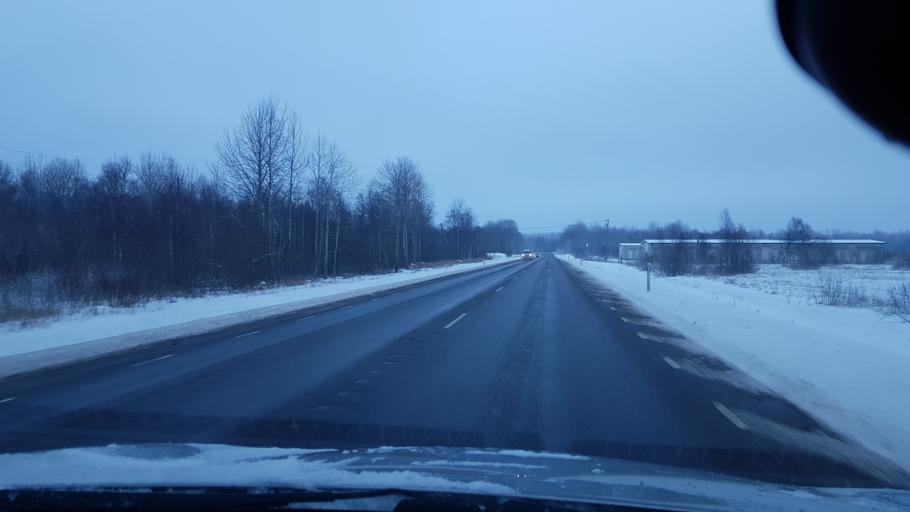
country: EE
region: Harju
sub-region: Paldiski linn
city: Paldiski
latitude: 59.3400
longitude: 24.1438
